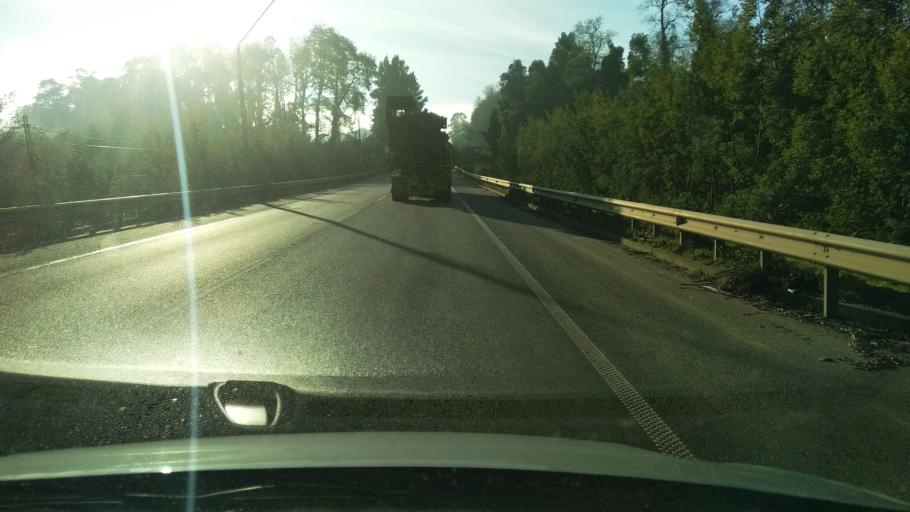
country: CL
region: Los Lagos
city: Las Animas
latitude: -39.7803
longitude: -73.2154
